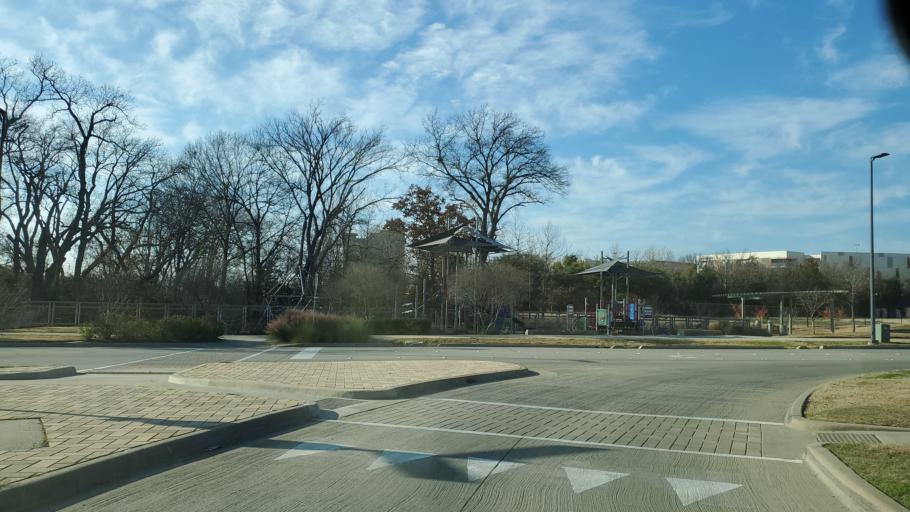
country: US
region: Texas
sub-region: Collin County
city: Plano
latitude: 32.9995
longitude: -96.7031
